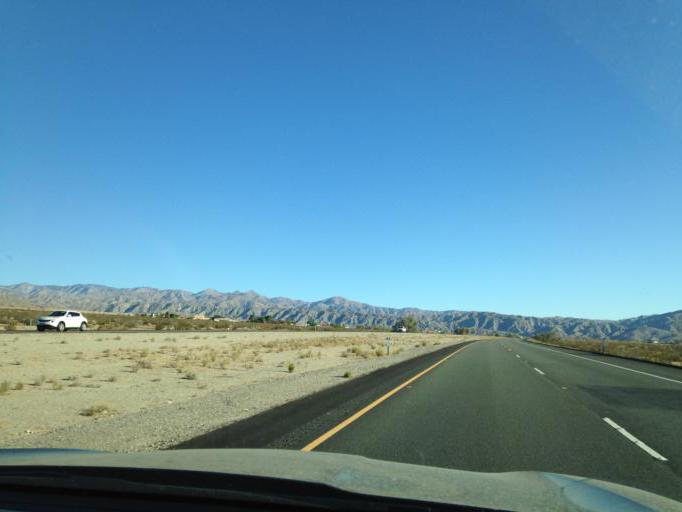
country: US
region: California
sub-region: Riverside County
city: Garnet
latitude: 33.9504
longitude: -116.5939
